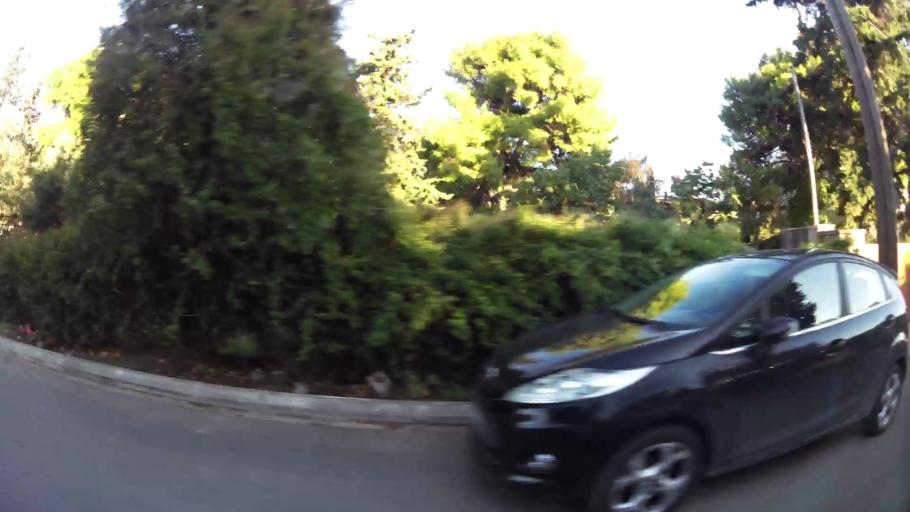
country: GR
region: Attica
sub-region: Nomarchia Anatolikis Attikis
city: Kryoneri
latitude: 38.1370
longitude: 23.8328
